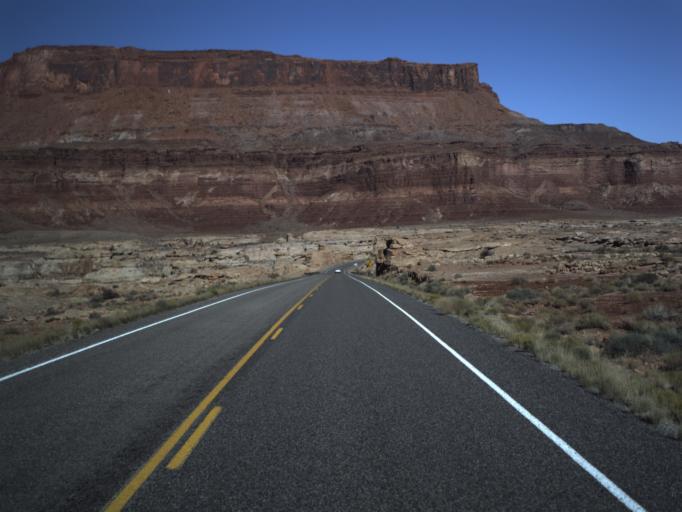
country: US
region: Utah
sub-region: San Juan County
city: Blanding
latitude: 37.9092
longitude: -110.3844
